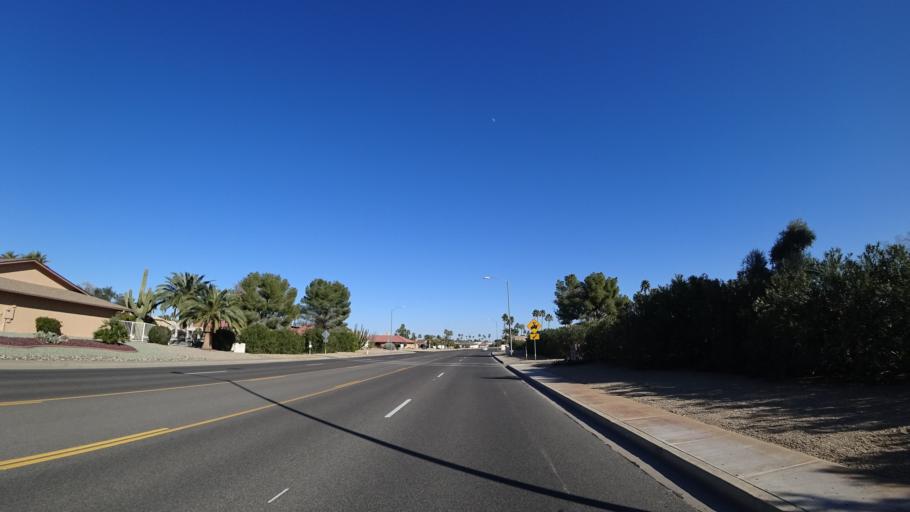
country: US
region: Arizona
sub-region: Maricopa County
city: Sun City West
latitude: 33.6787
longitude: -112.3500
